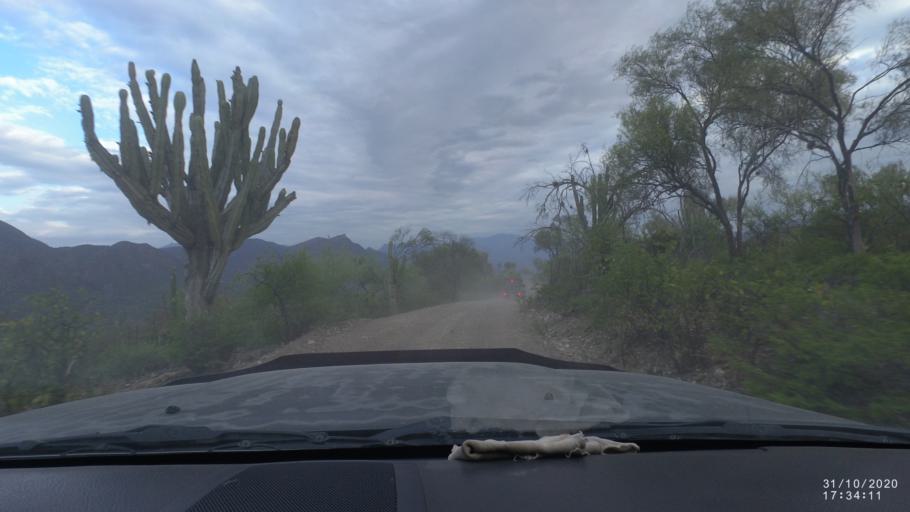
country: BO
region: Chuquisaca
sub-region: Provincia Zudanez
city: Mojocoya
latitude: -18.6004
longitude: -64.5482
